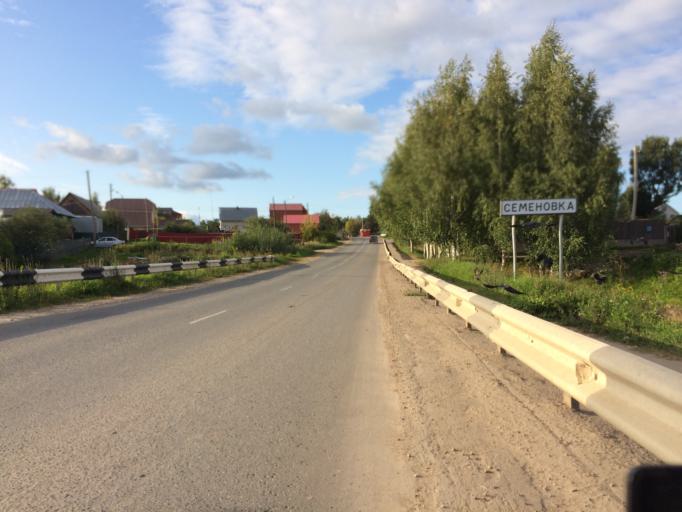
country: RU
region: Mariy-El
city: Yoshkar-Ola
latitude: 56.6487
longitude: 47.9808
